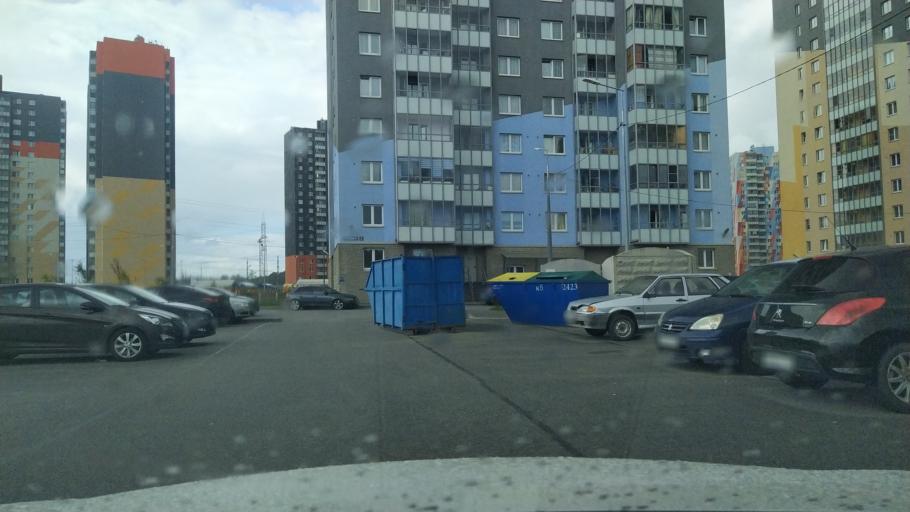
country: RU
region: Leningrad
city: Murino
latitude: 60.0272
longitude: 30.4574
